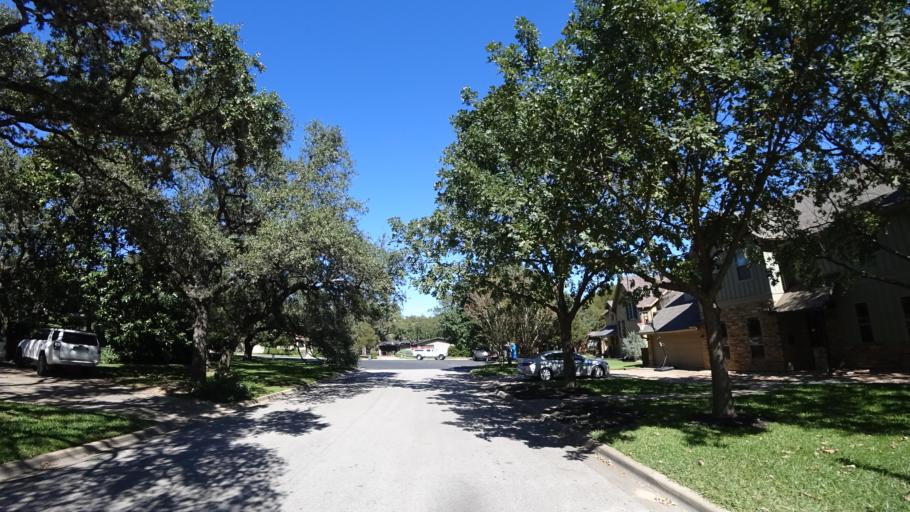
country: US
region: Texas
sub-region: Travis County
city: West Lake Hills
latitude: 30.3275
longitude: -97.7642
